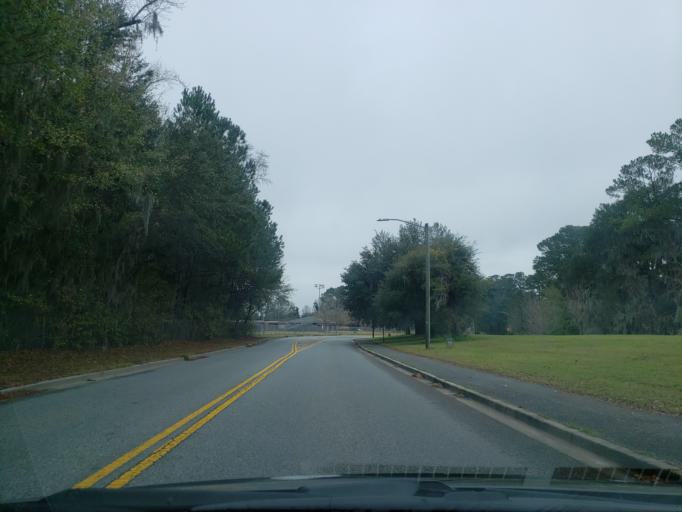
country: US
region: Georgia
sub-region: Chatham County
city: Montgomery
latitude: 31.9740
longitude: -81.1609
